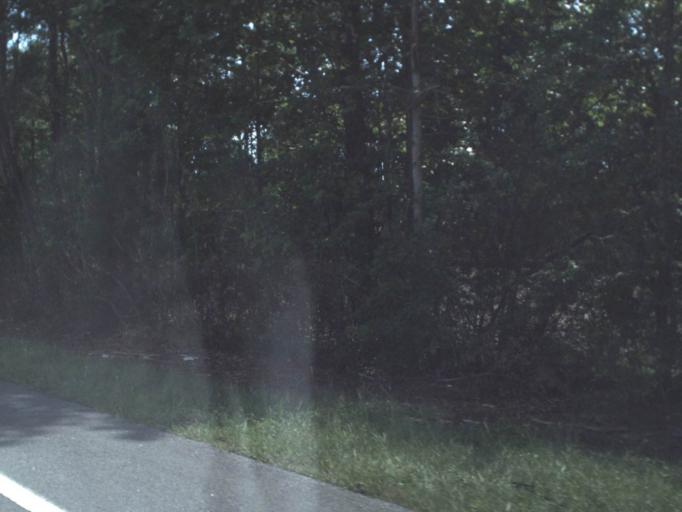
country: US
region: Florida
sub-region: Nassau County
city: Yulee
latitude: 30.5072
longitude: -81.6229
